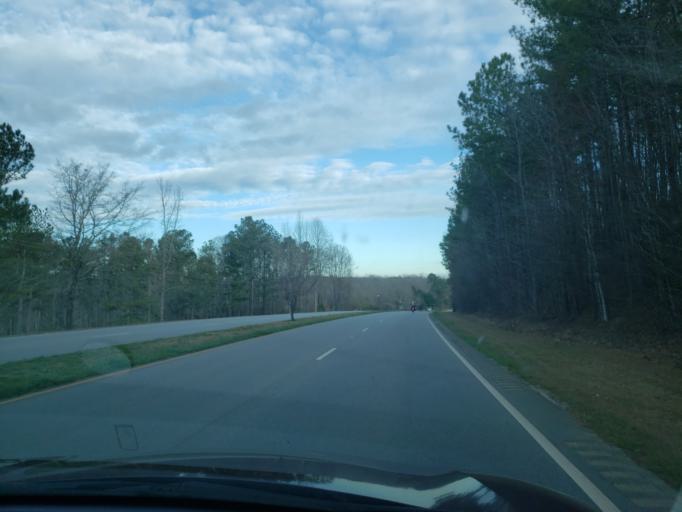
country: US
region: Alabama
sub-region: Randolph County
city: Wedowee
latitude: 33.3008
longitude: -85.4829
